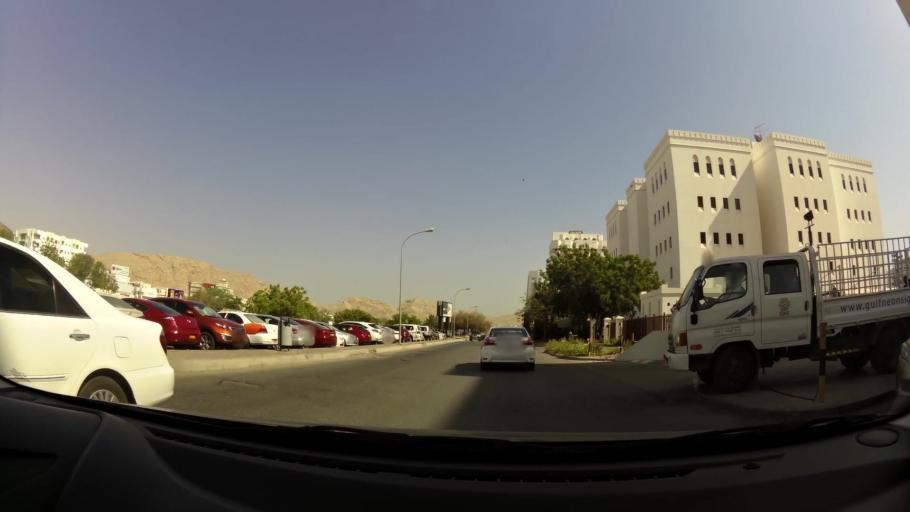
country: OM
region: Muhafazat Masqat
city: Muscat
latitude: 23.5948
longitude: 58.5487
